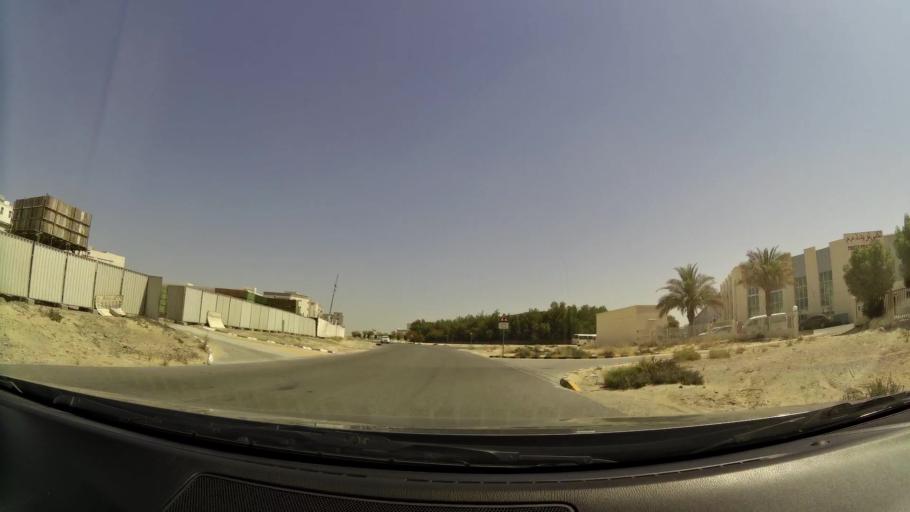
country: AE
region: Dubai
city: Dubai
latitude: 24.9729
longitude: 55.2076
